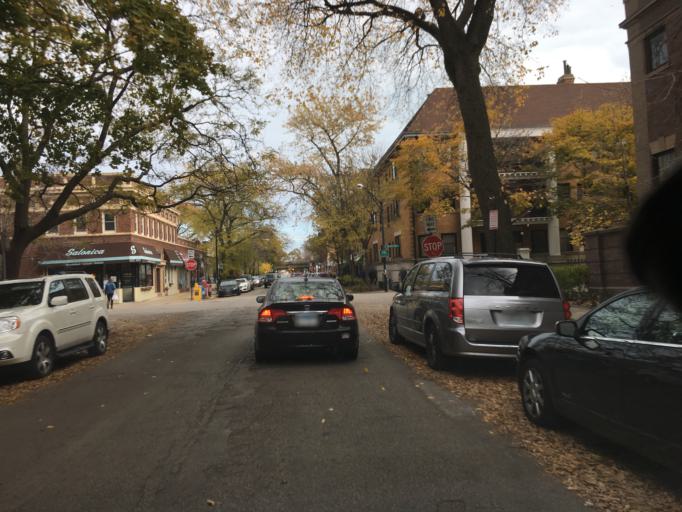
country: US
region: Illinois
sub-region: Cook County
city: Chicago
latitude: 41.7915
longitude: -87.5907
